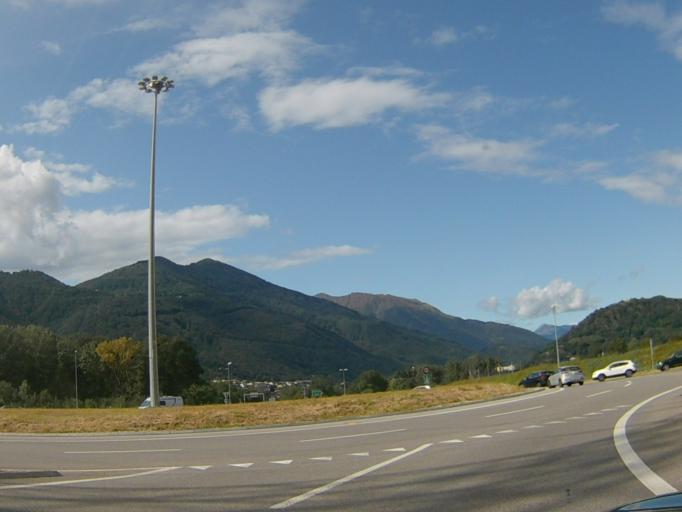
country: CH
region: Ticino
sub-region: Lugano District
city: Cadempino
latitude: 46.0271
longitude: 8.9314
